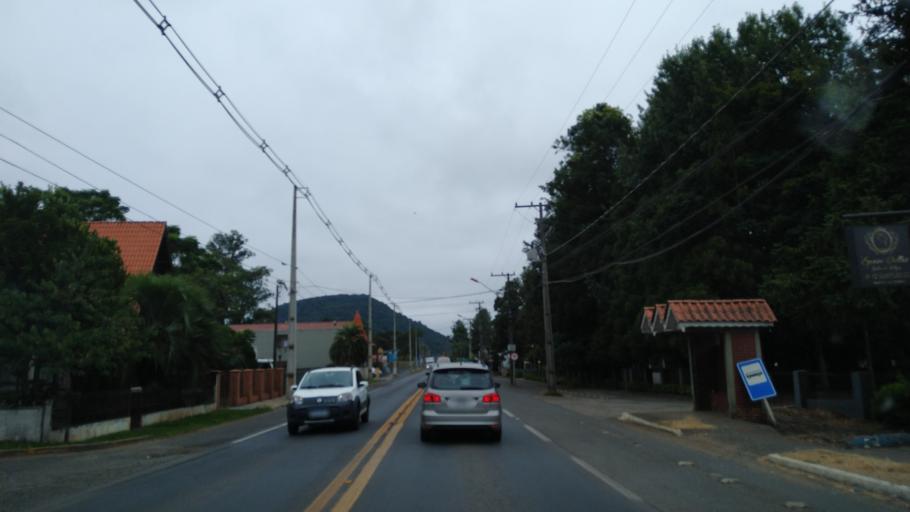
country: BR
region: Santa Catarina
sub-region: Porto Uniao
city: Porto Uniao
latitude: -26.2607
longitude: -51.0649
